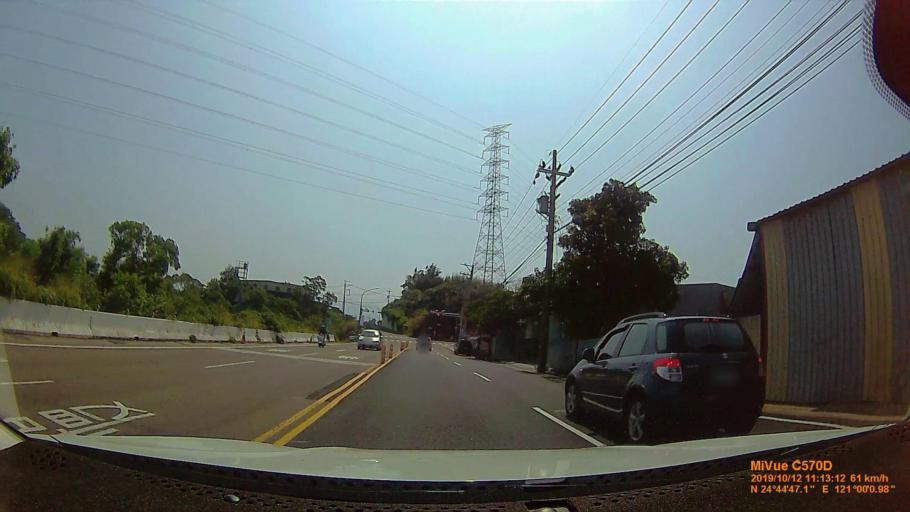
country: TW
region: Taiwan
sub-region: Hsinchu
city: Hsinchu
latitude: 24.7462
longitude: 121.0003
